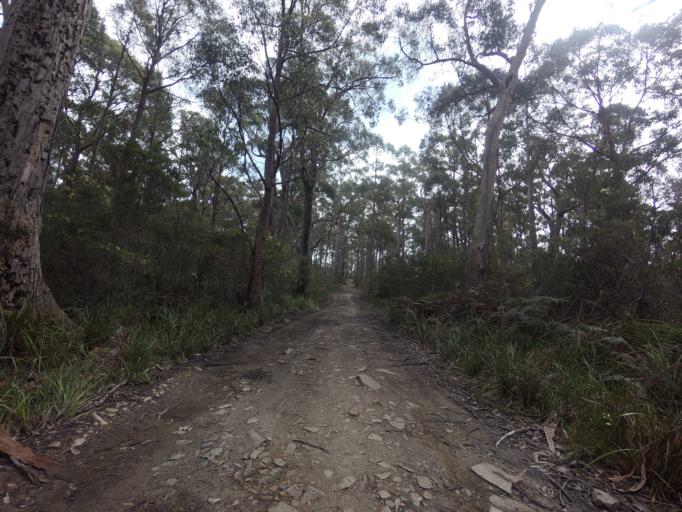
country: AU
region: Tasmania
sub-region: Huon Valley
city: Geeveston
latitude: -43.4667
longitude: 146.9307
